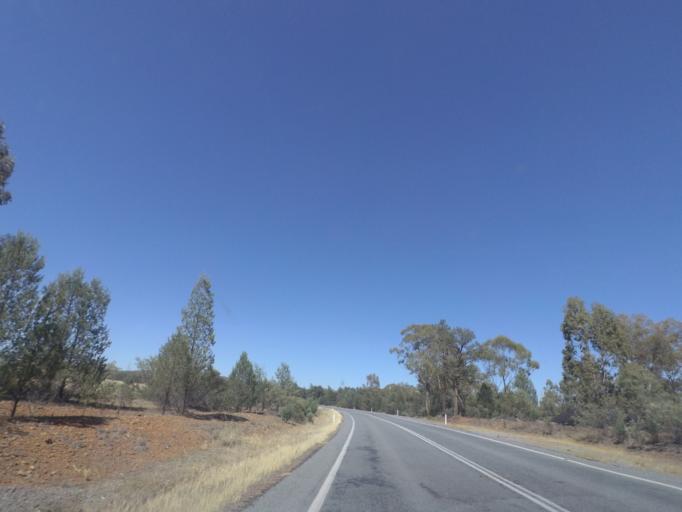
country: AU
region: New South Wales
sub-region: Narrandera
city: Narrandera
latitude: -34.4190
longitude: 146.8485
